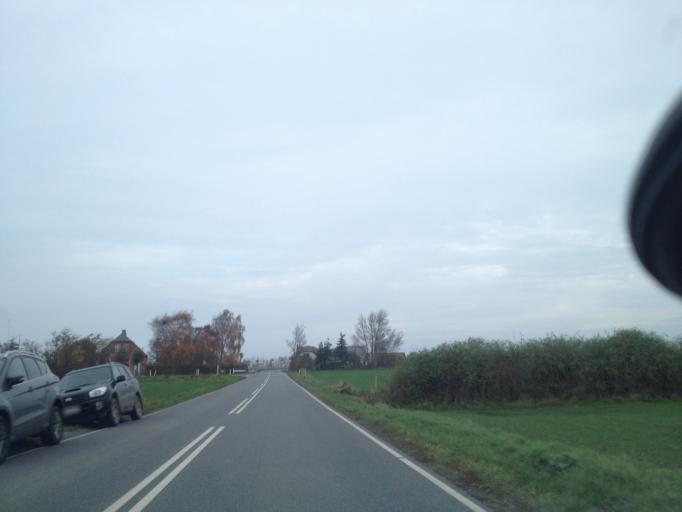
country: DK
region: South Denmark
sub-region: Nordfyns Kommune
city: Bogense
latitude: 55.5339
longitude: 10.0973
